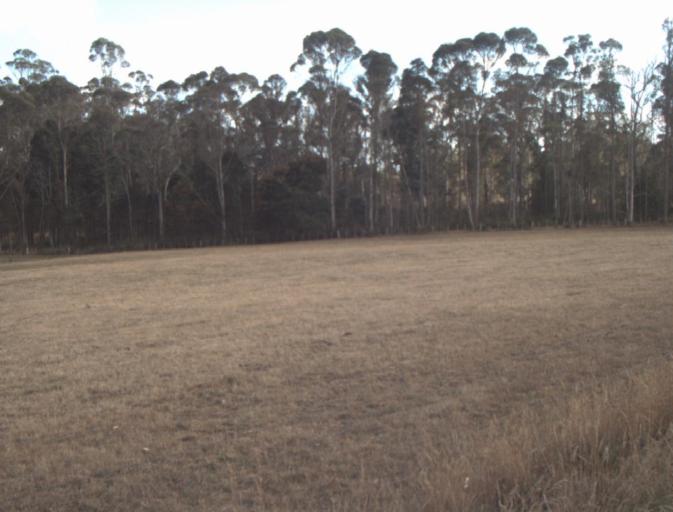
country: AU
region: Tasmania
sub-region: Dorset
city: Bridport
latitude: -41.1255
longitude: 147.2031
